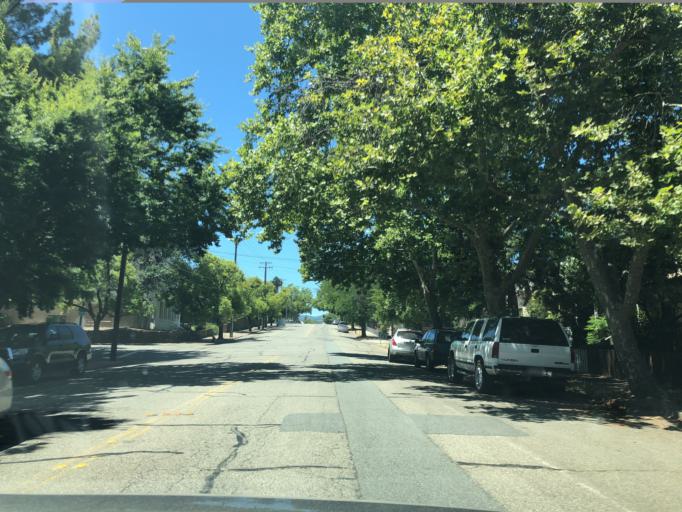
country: US
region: California
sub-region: Shasta County
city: Redding
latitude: 40.5895
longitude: -122.3893
